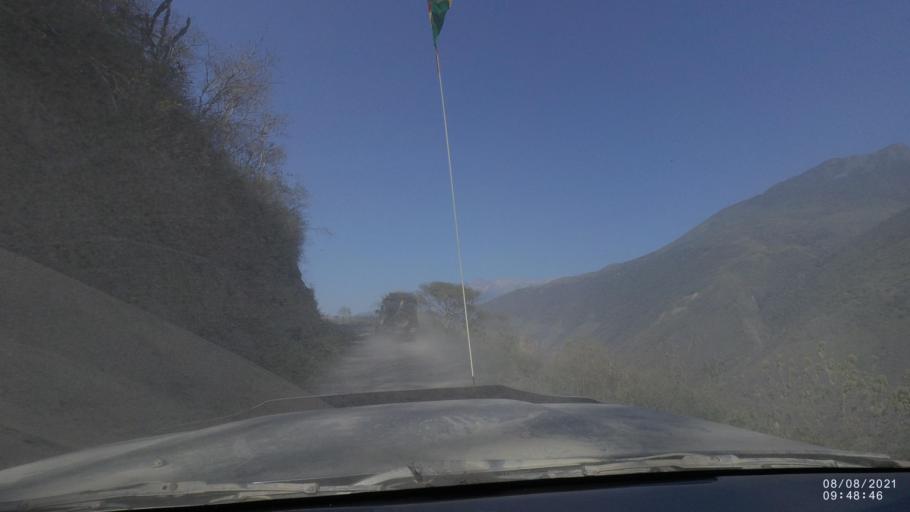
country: BO
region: La Paz
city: Quime
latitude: -16.6142
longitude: -66.7293
